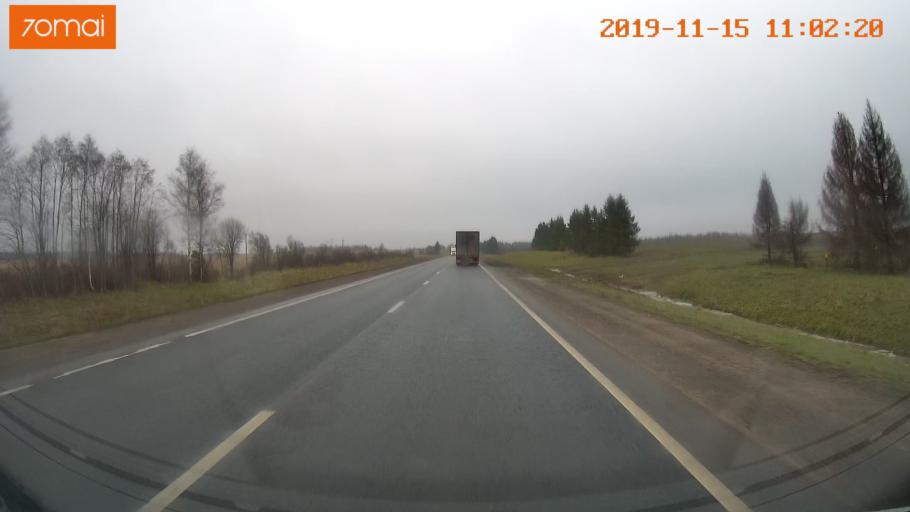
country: RU
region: Vologda
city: Chebsara
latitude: 59.1292
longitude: 38.9386
